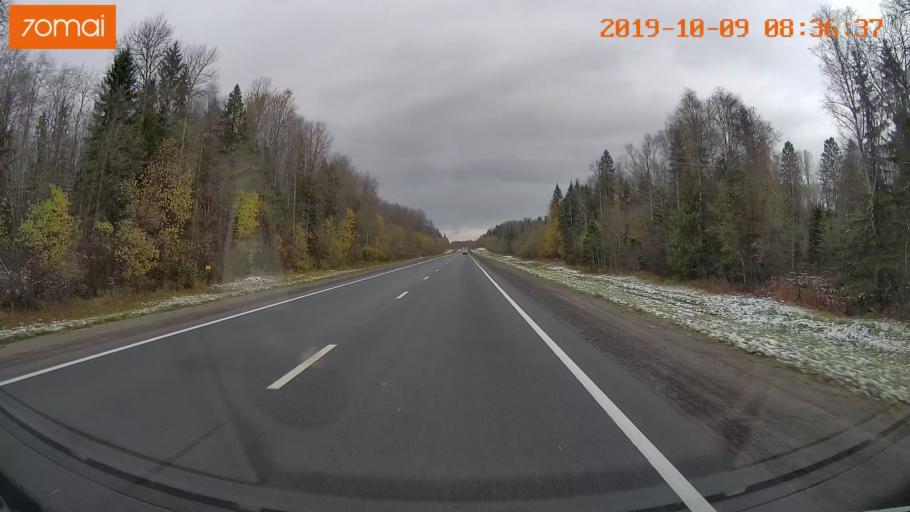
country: RU
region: Vologda
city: Gryazovets
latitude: 58.9291
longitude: 40.1761
